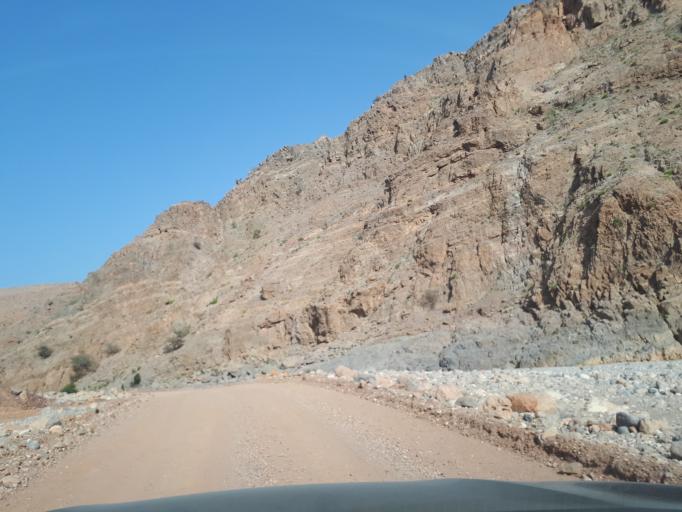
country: OM
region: Ash Sharqiyah
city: Al Qabil
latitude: 23.0671
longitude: 59.0072
